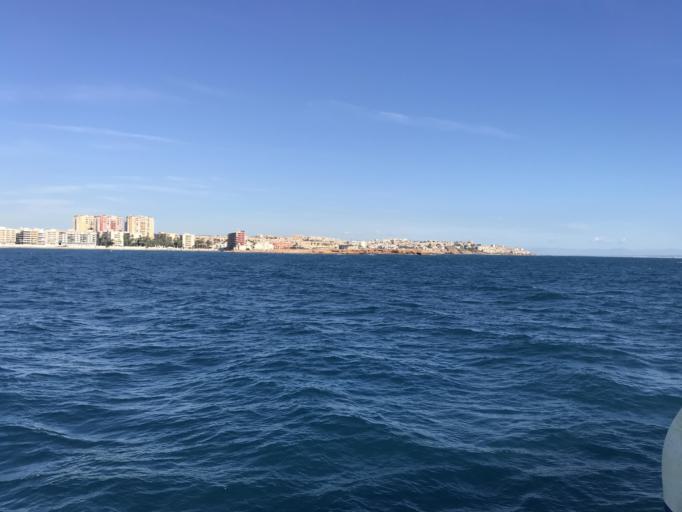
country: ES
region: Valencia
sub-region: Provincia de Alicante
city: Torrevieja
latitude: 37.9772
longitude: -0.6552
